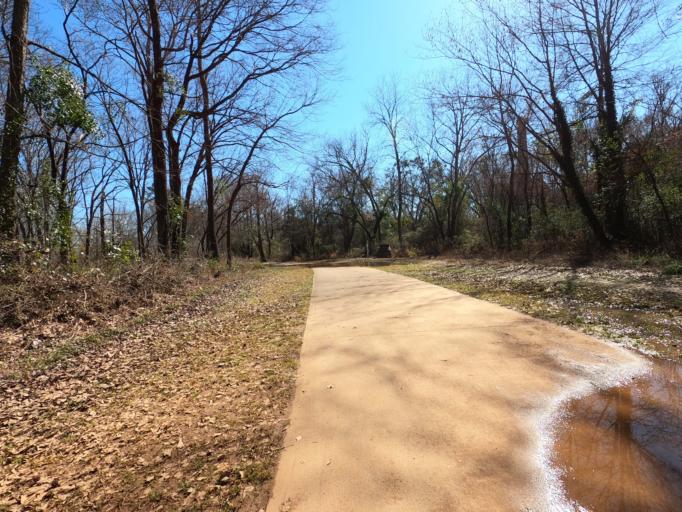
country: US
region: Georgia
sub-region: Clarke County
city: Athens
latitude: 33.9707
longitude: -83.3790
